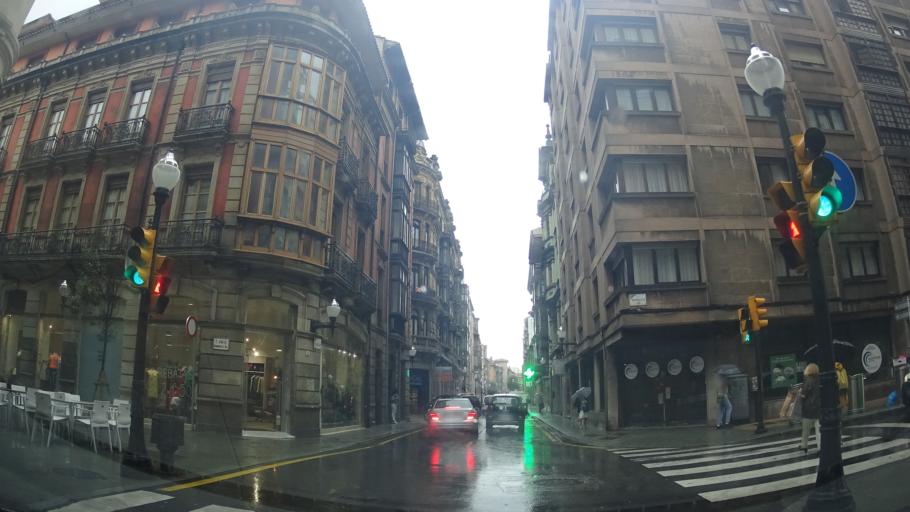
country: ES
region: Asturias
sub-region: Province of Asturias
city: Gijon
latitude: 43.5423
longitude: -5.6617
